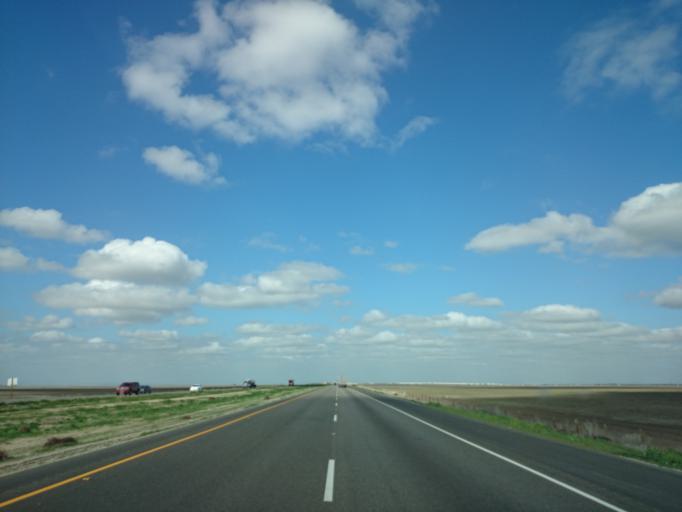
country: US
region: California
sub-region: Kern County
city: Greenfield
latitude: 35.1332
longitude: -119.0792
